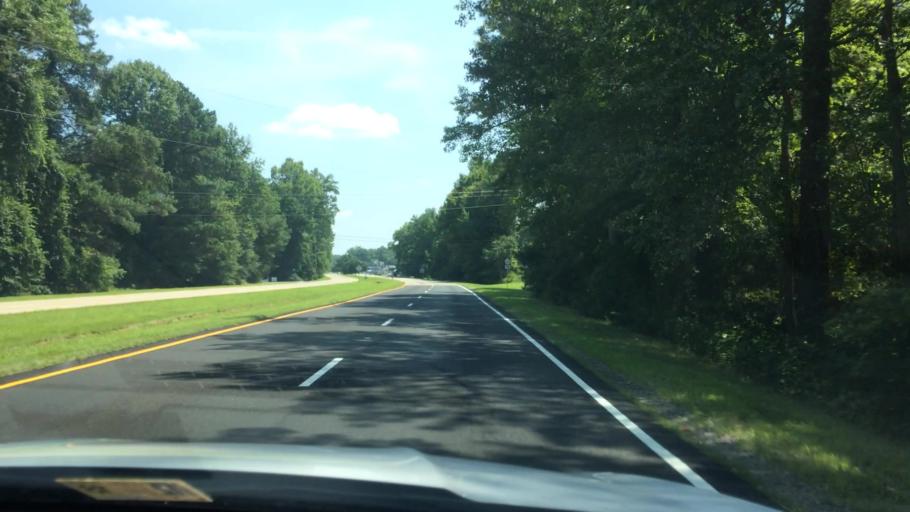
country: US
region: Virginia
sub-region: Charles City County
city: Charles City
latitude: 37.4429
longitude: -77.0497
